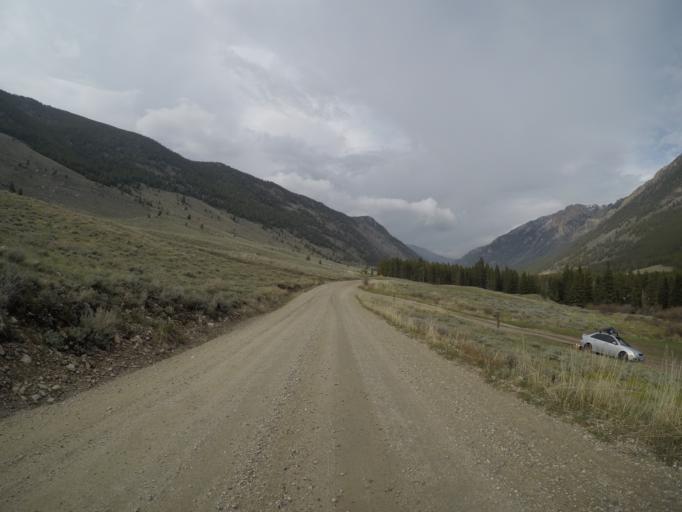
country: US
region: Montana
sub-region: Carbon County
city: Red Lodge
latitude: 45.0553
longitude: -109.4174
